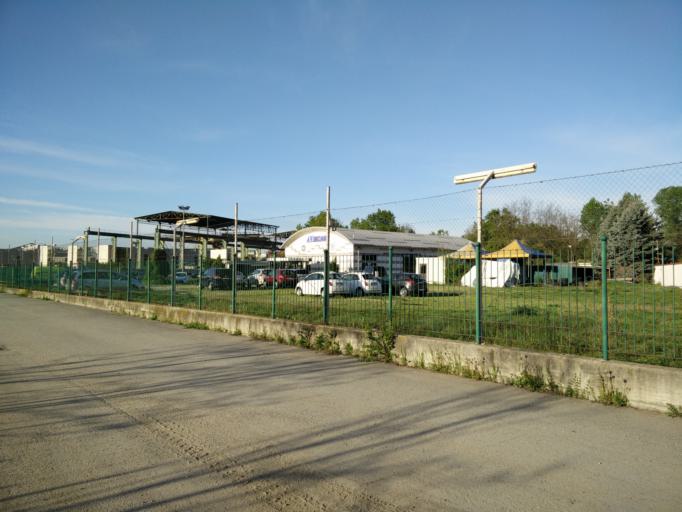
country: IT
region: Piedmont
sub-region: Provincia di Torino
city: Borgo Melano
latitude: 45.0203
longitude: 7.5726
